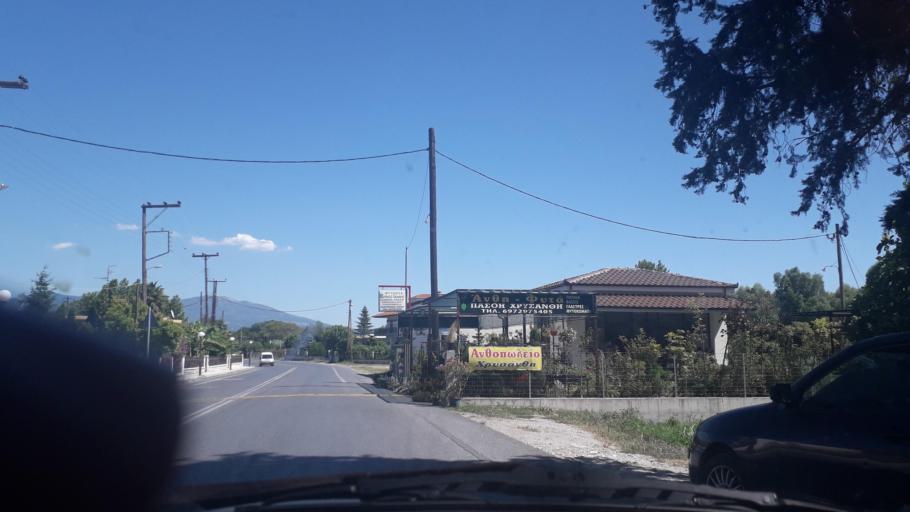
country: GR
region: Central Macedonia
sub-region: Nomos Pellis
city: Tsakoi
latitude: 40.9690
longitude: 22.0195
